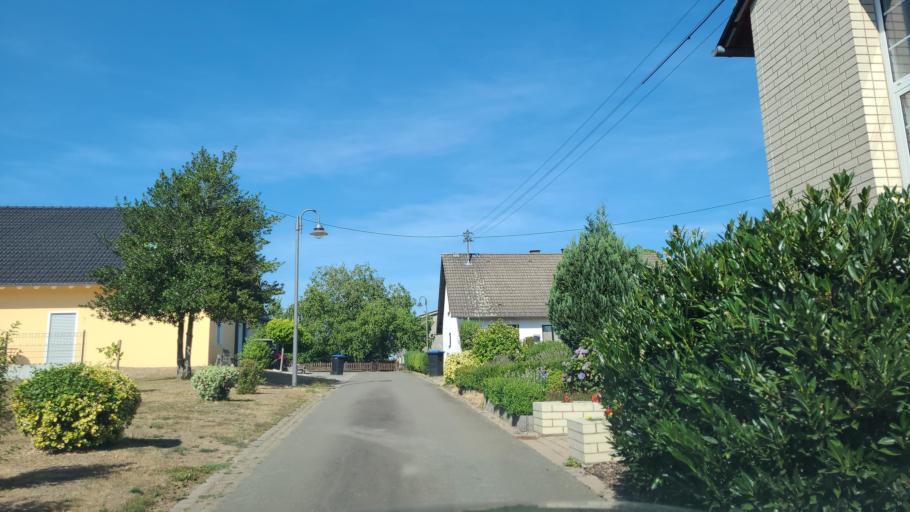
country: DE
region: Rheinland-Pfalz
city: Burtscheid
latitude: 49.7322
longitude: 6.9582
